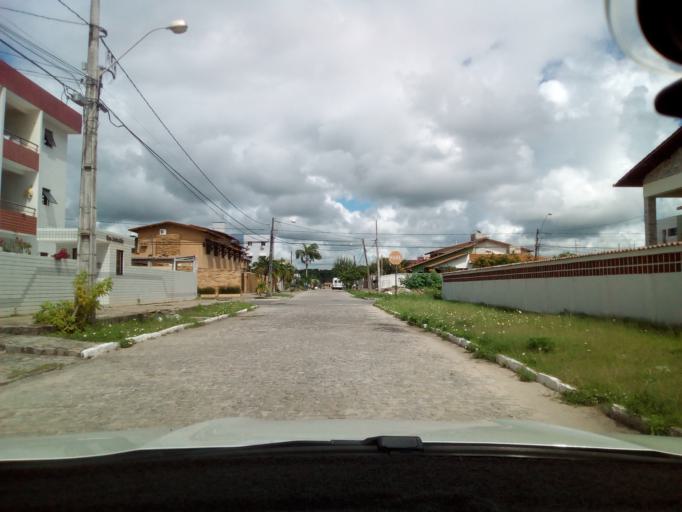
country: BR
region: Paraiba
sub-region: Joao Pessoa
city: Joao Pessoa
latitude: -7.0647
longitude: -34.8450
